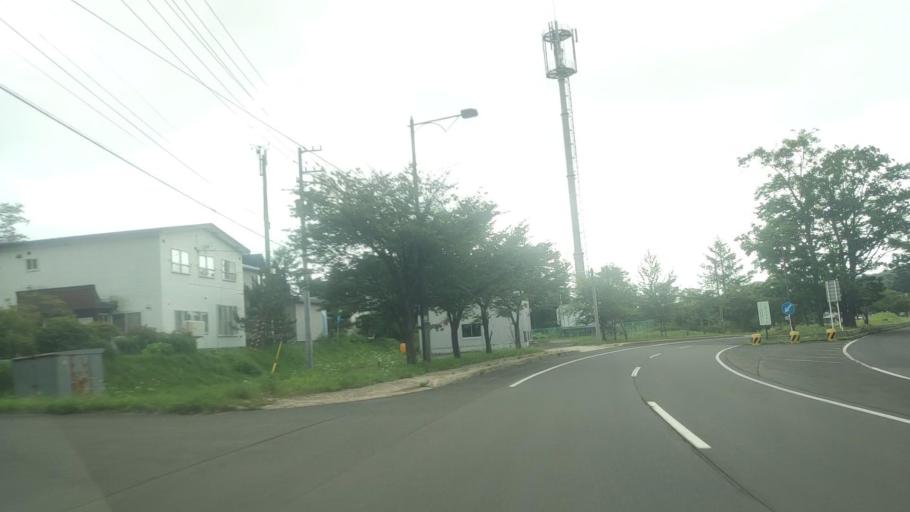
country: JP
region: Hokkaido
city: Shiraoi
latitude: 42.4709
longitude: 141.1594
